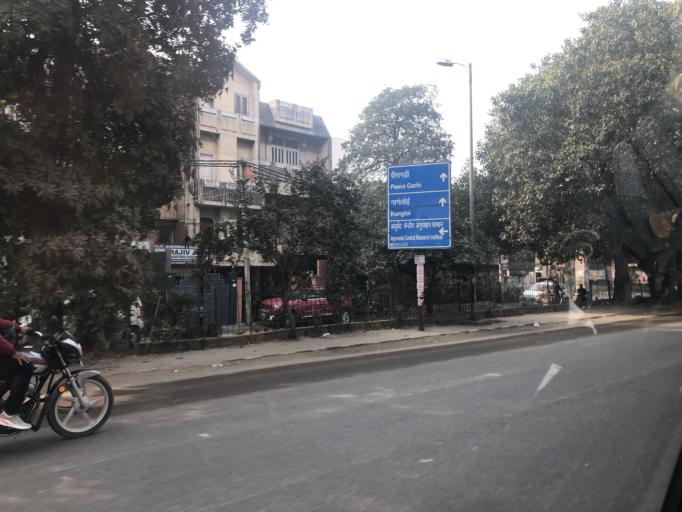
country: IN
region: NCT
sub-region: North West Delhi
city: Pitampura
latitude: 28.6757
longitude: 77.1248
